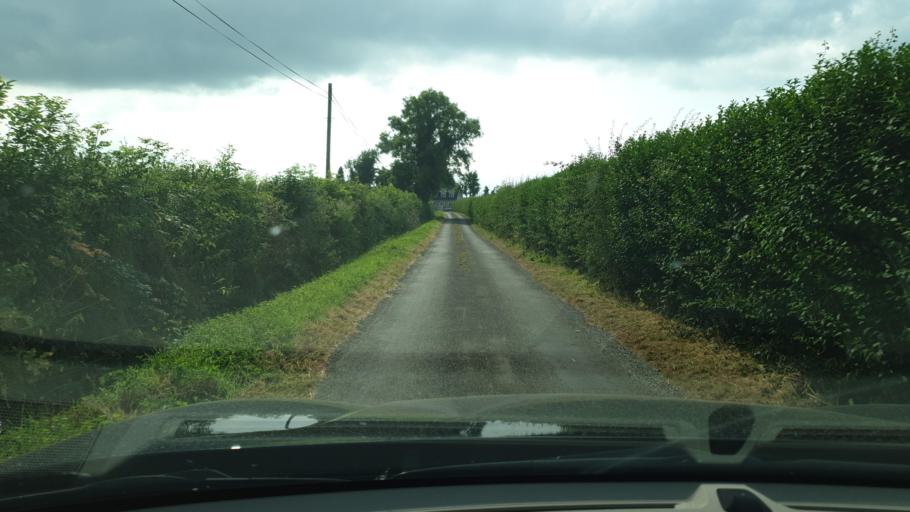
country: IE
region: Leinster
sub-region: An Mhi
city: Ratoath
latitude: 53.4734
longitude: -6.4475
